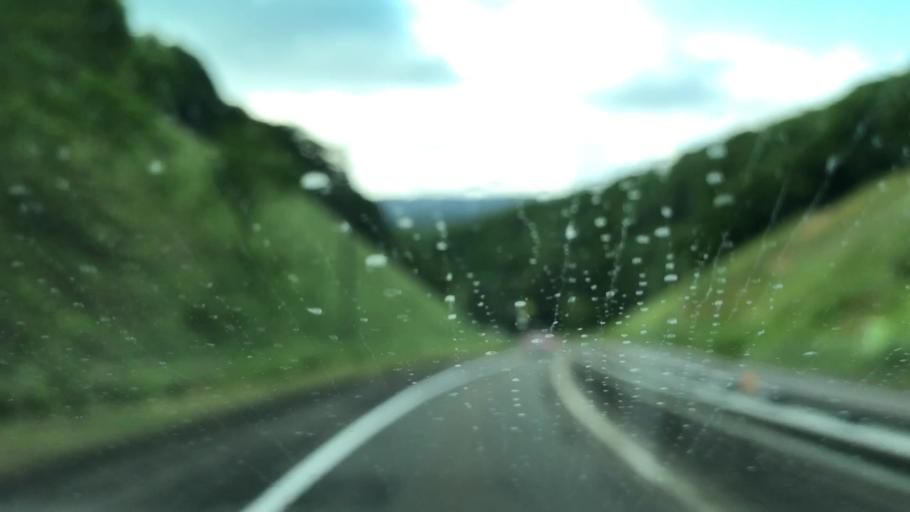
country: JP
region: Hokkaido
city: Shimo-furano
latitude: 42.8850
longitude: 142.2634
